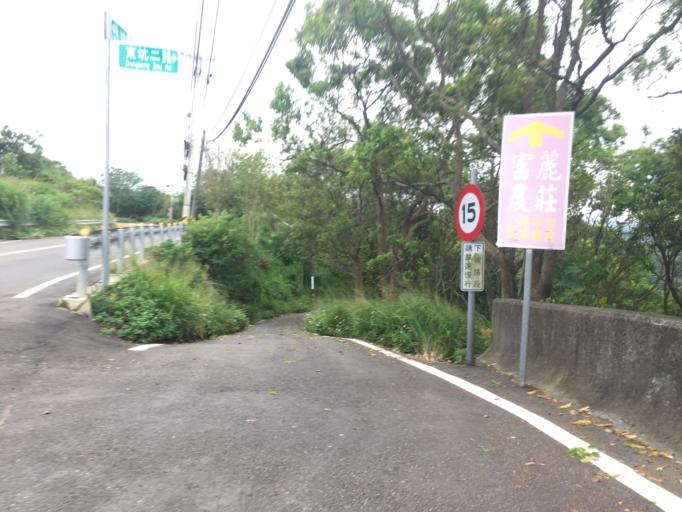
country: TW
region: Taiwan
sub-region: Hsinchu
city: Hsinchu
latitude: 24.7410
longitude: 120.9828
